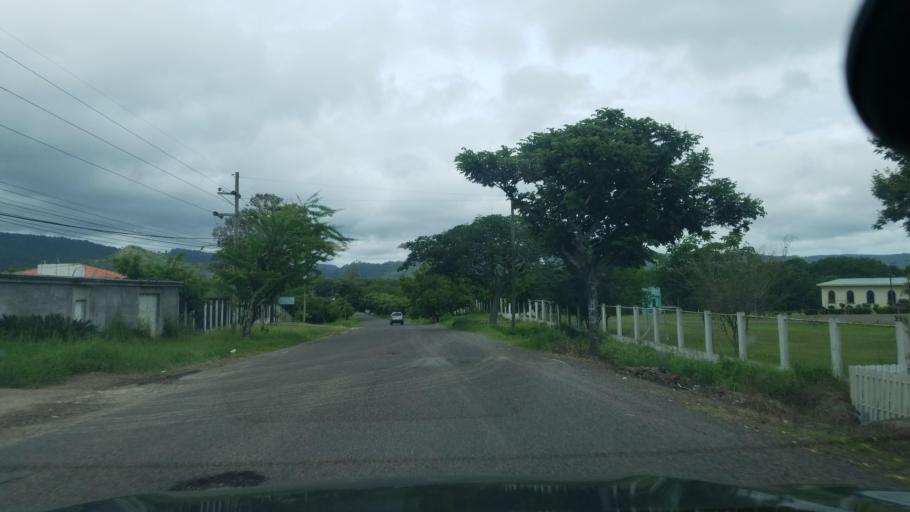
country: HN
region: Choluteca
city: San Marcos de Colon
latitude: 13.4126
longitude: -86.8415
